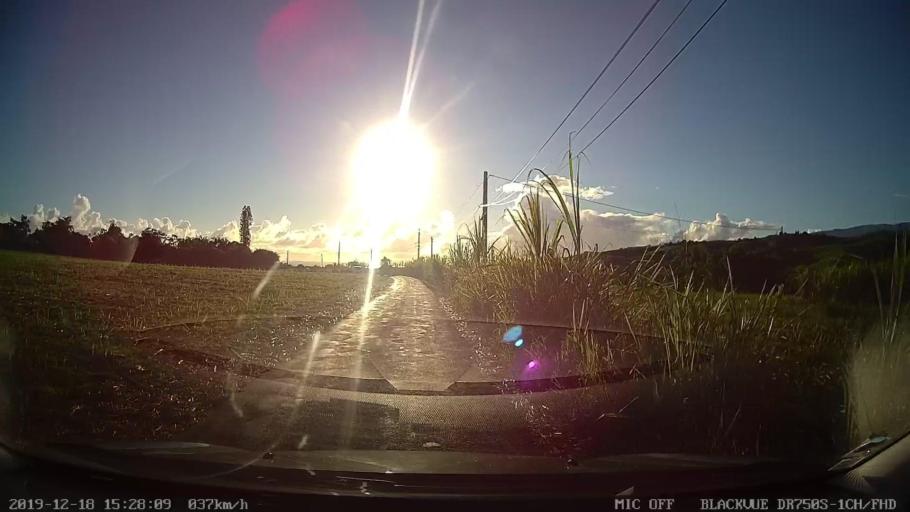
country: RE
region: Reunion
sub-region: Reunion
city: Bras-Panon
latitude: -20.9987
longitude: 55.6567
